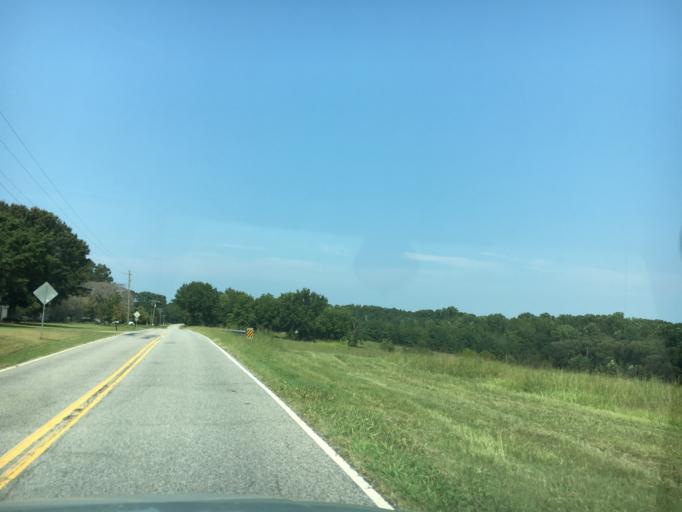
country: US
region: South Carolina
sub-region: Spartanburg County
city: Mayo
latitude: 35.1331
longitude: -81.9117
